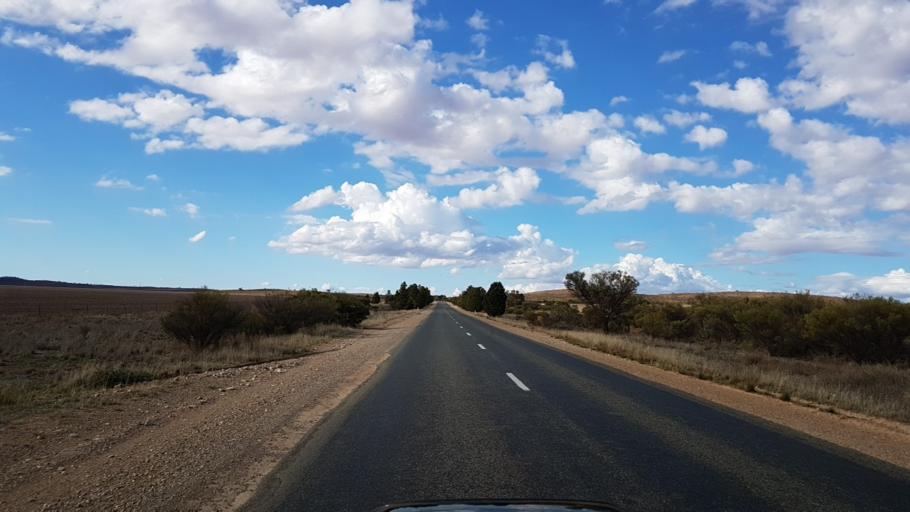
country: AU
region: South Australia
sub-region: Peterborough
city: Peterborough
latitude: -32.9635
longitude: 138.8829
